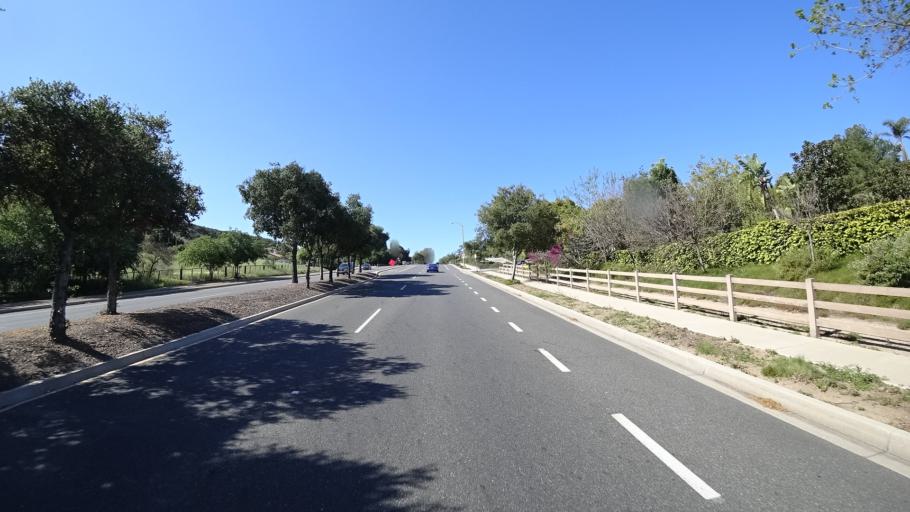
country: US
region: California
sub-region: Ventura County
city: Casa Conejo
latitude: 34.1704
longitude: -118.9353
